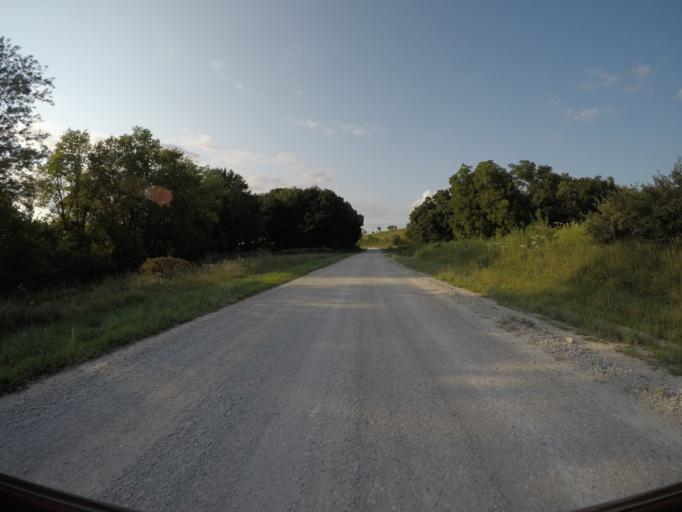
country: US
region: Kansas
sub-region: Wabaunsee County
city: Alma
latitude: 38.9704
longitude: -96.2626
